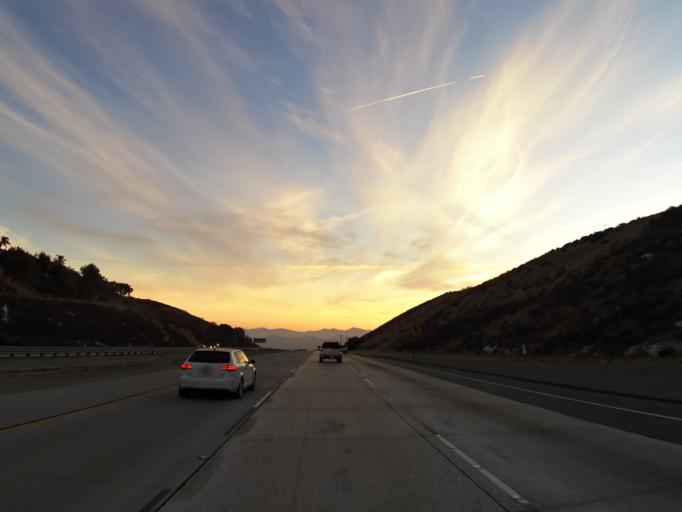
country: US
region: California
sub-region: Ventura County
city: Thousand Oaks
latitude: 34.2264
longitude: -118.8479
